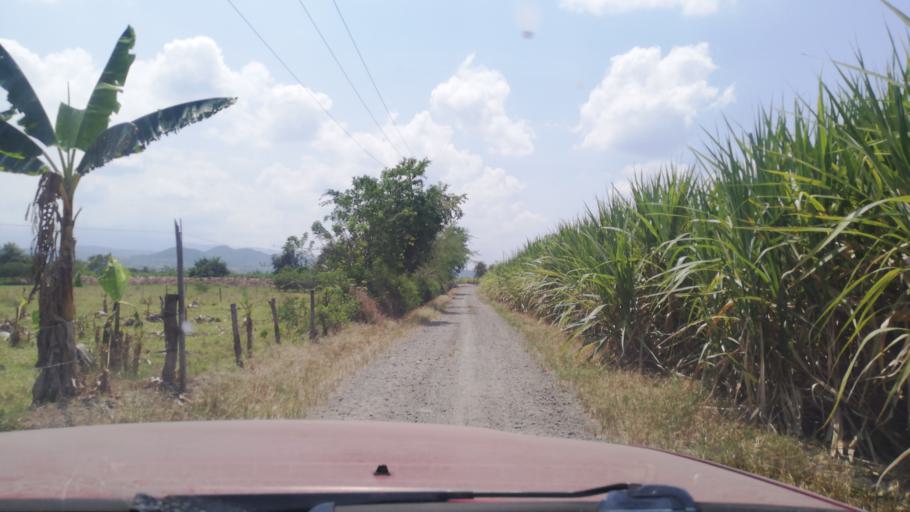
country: CO
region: Valle del Cauca
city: San Pedro
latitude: 3.9916
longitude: -76.2642
